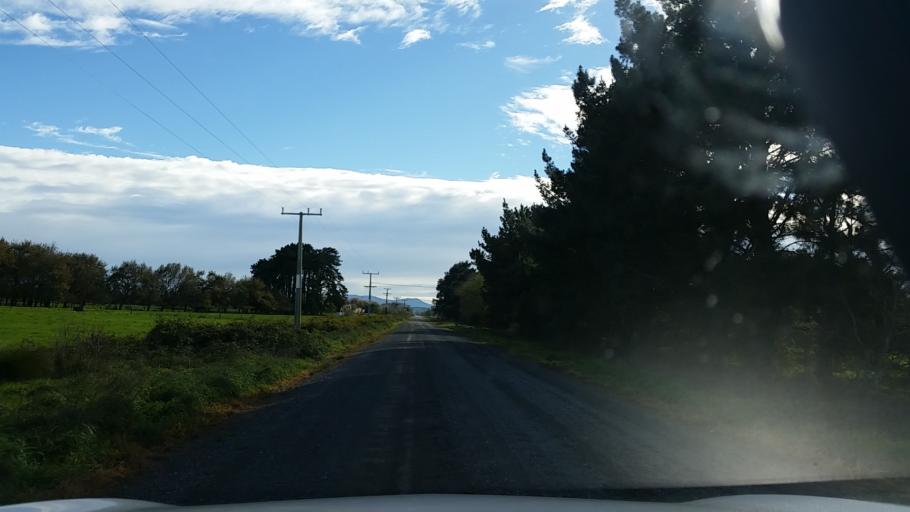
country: NZ
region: Waikato
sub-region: Hamilton City
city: Hamilton
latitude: -37.6589
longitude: 175.4367
